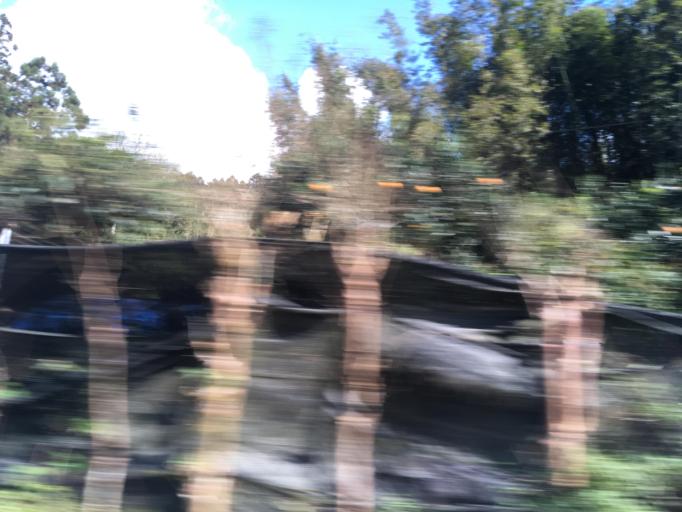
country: TW
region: Taiwan
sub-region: Yilan
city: Yilan
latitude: 24.7511
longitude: 121.6256
